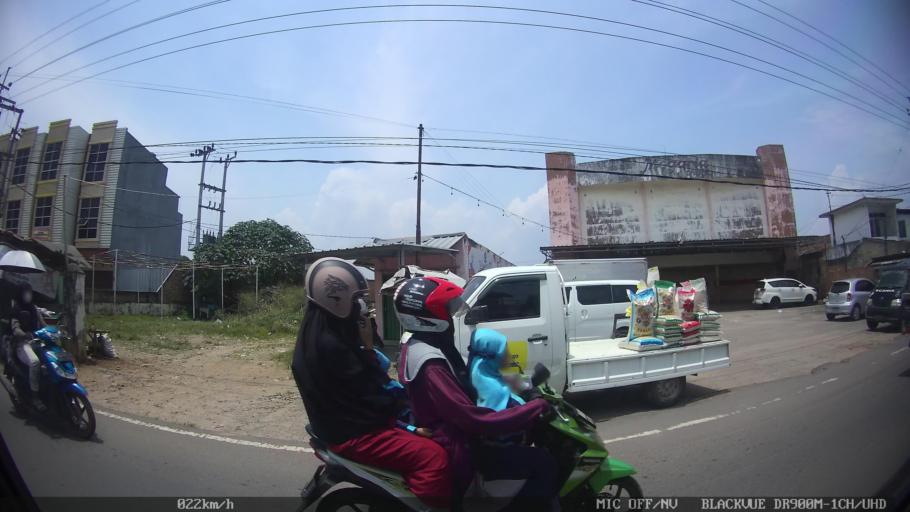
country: ID
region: Lampung
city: Bandarlampung
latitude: -5.4484
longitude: 105.2568
